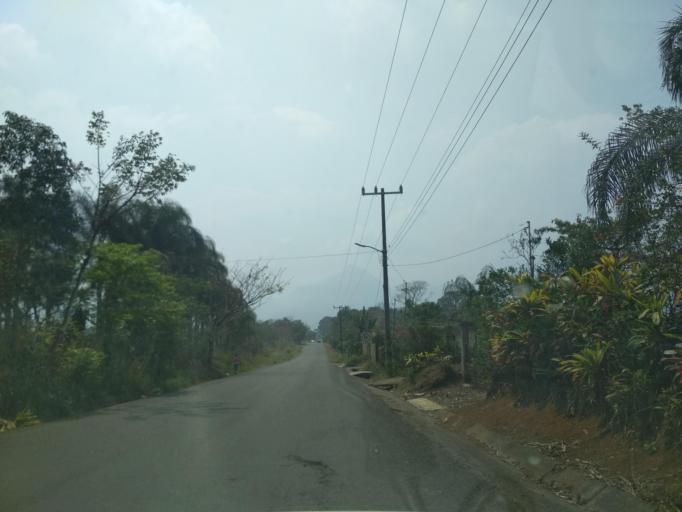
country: MX
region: Veracruz
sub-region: Cordoba
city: Fredepo
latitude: 18.8622
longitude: -96.9841
